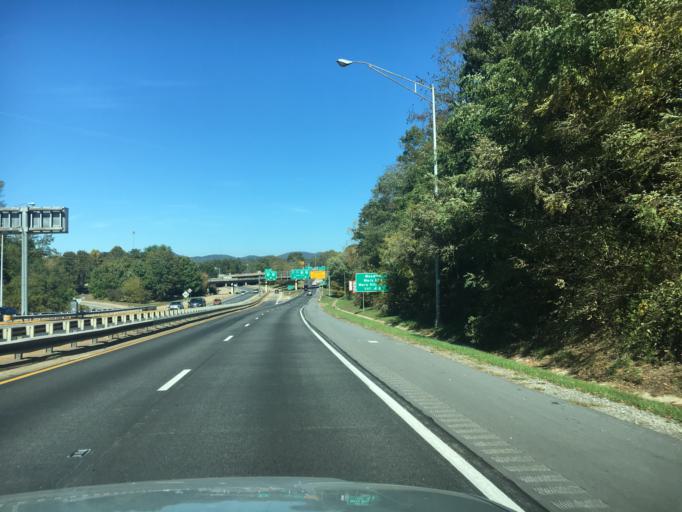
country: US
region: North Carolina
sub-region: Buncombe County
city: Asheville
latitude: 35.5853
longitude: -82.5818
